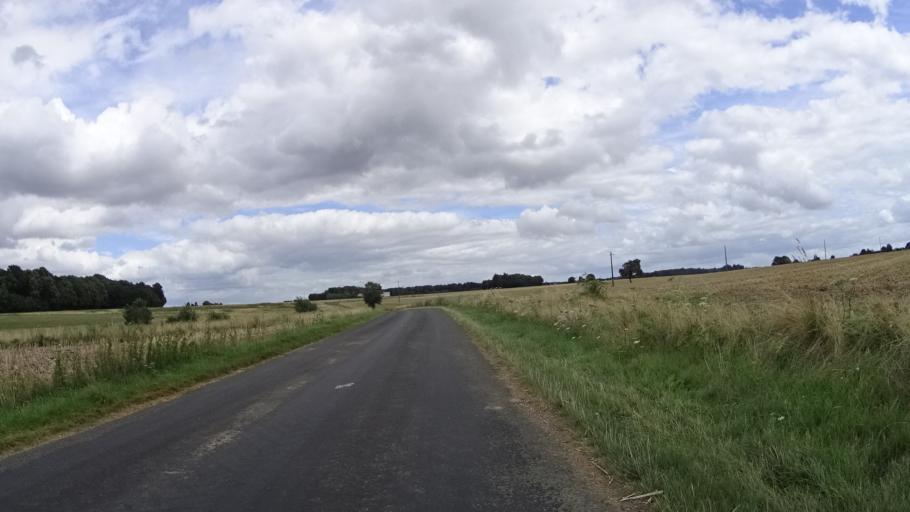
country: FR
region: Centre
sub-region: Departement du Loiret
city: Douchy
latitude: 47.9721
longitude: 3.0798
